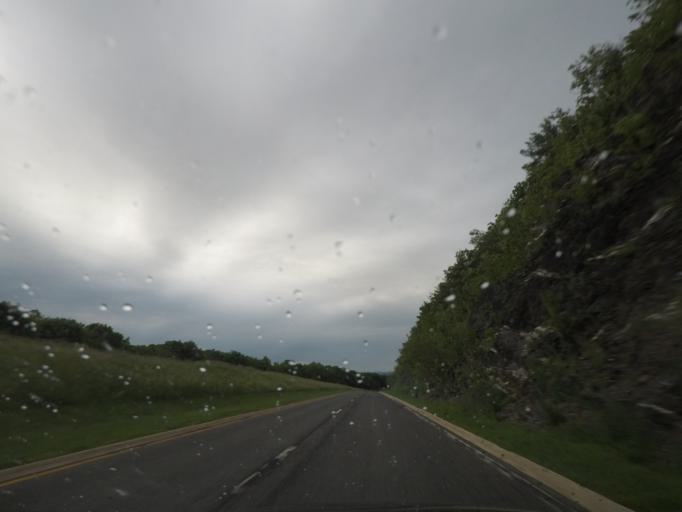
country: US
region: New York
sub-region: Columbia County
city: Chatham
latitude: 42.3208
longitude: -73.5758
